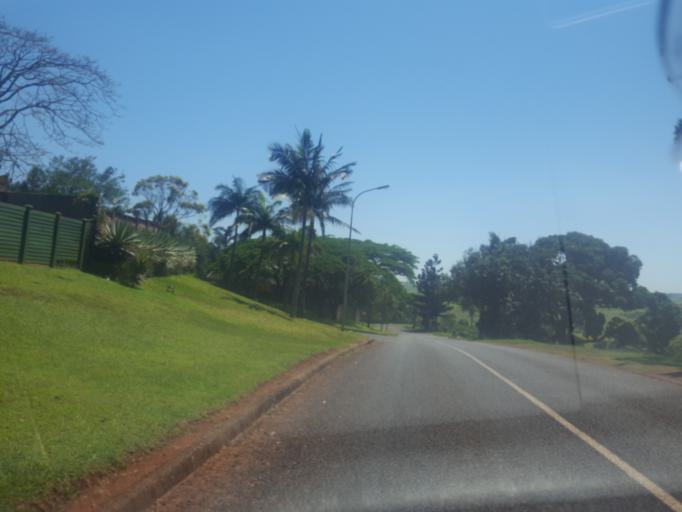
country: ZA
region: KwaZulu-Natal
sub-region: uThungulu District Municipality
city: Empangeni
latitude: -28.7499
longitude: 31.9083
